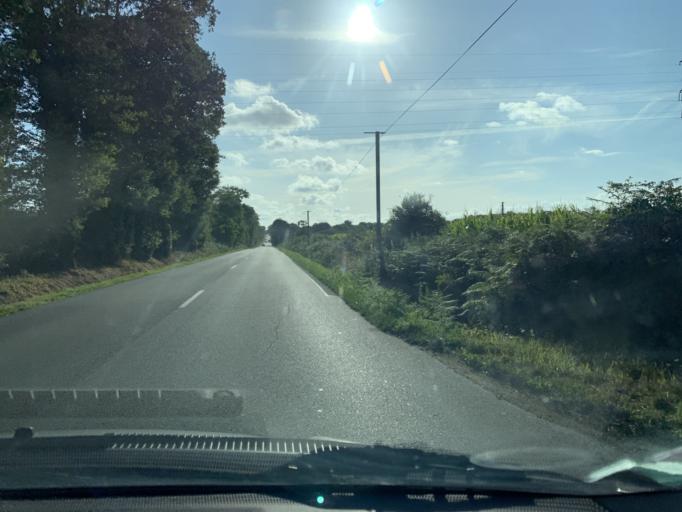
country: FR
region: Brittany
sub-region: Departement du Morbihan
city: Ambon
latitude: 47.5566
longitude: -2.5224
